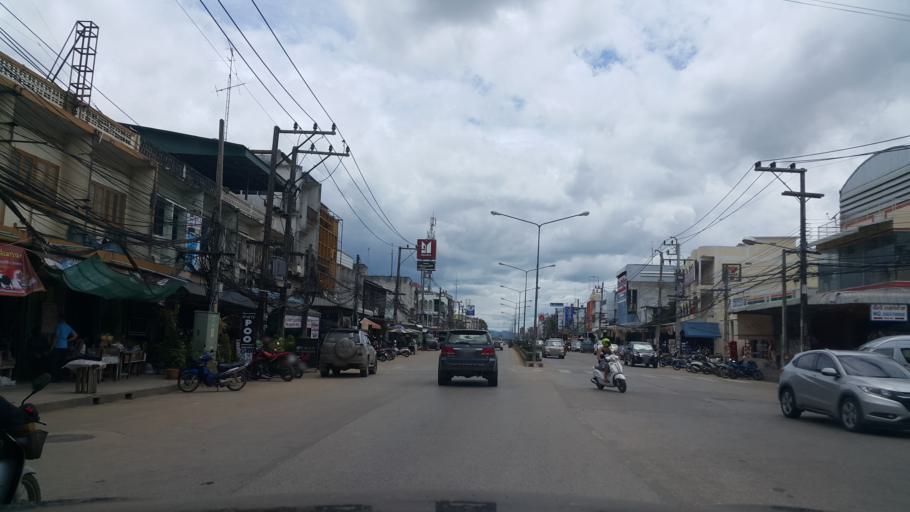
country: TH
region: Sukhothai
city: Sukhothai
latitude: 17.0084
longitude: 99.8154
